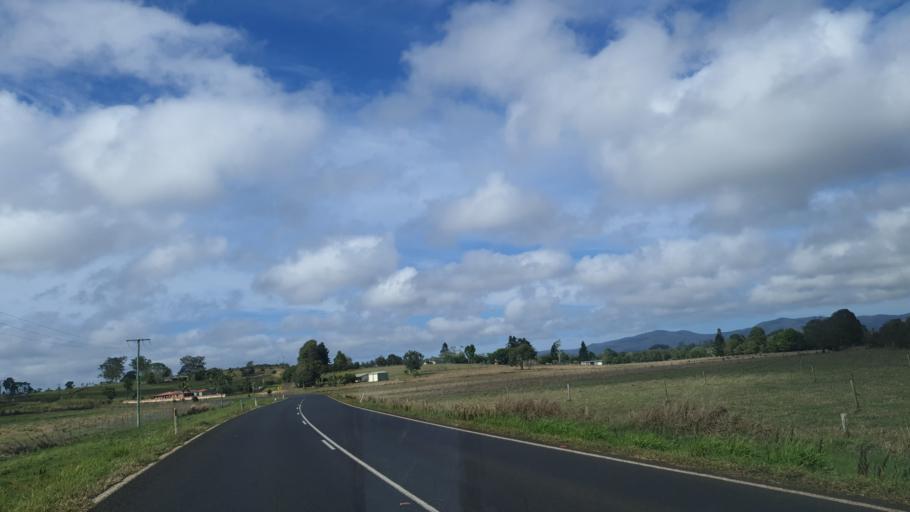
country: AU
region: Queensland
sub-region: Tablelands
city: Atherton
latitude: -17.3079
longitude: 145.5542
